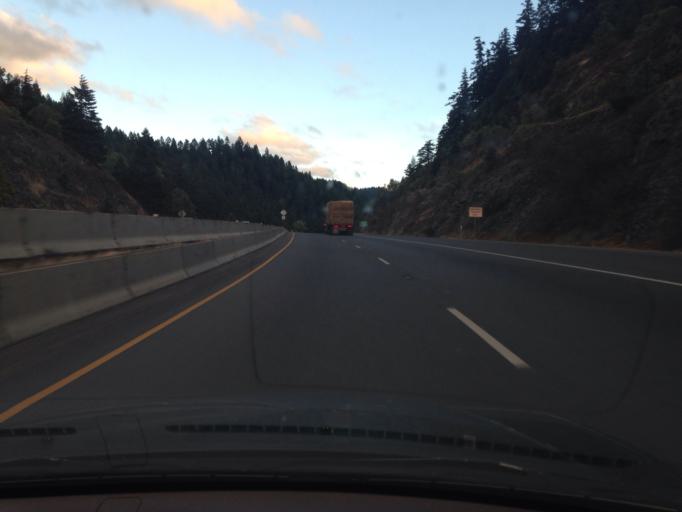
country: US
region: Oregon
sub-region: Douglas County
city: Canyonville
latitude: 42.7334
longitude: -123.3710
